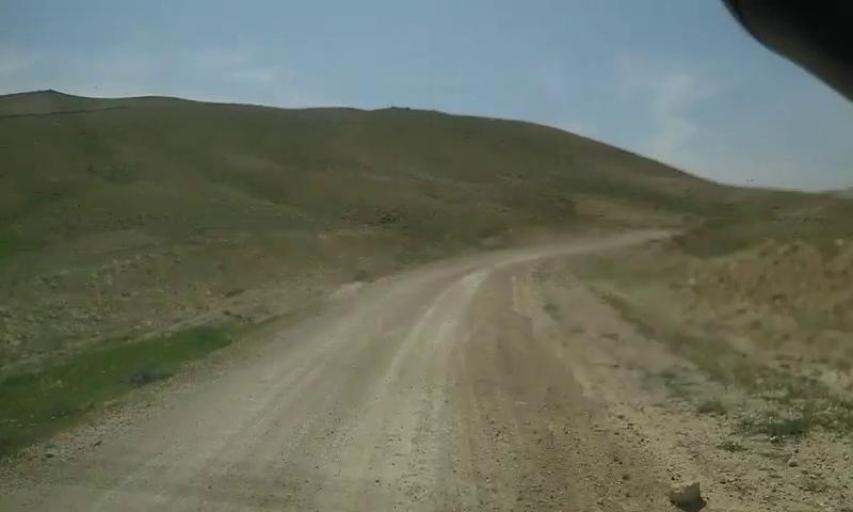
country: PS
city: `Arab ar Rashaydah
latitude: 31.4834
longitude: 35.2788
